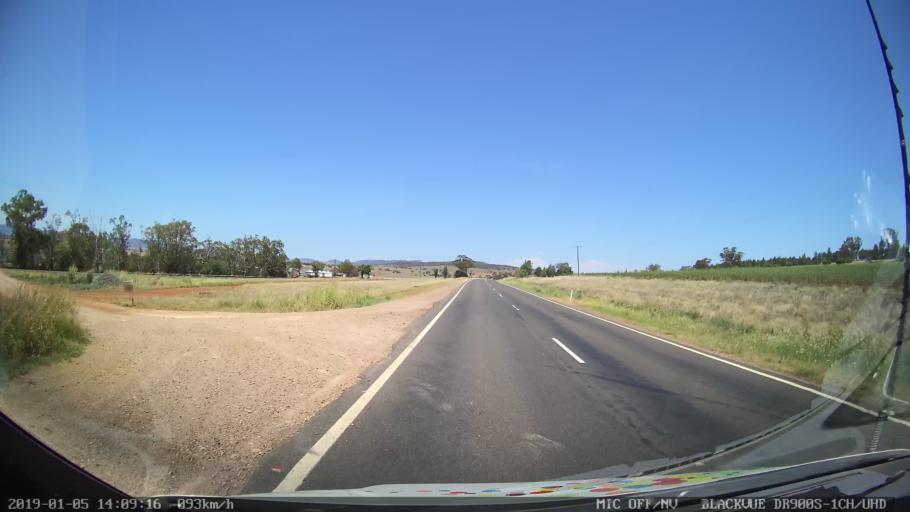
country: AU
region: New South Wales
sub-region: Gunnedah
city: Gunnedah
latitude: -31.2411
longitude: 150.4248
